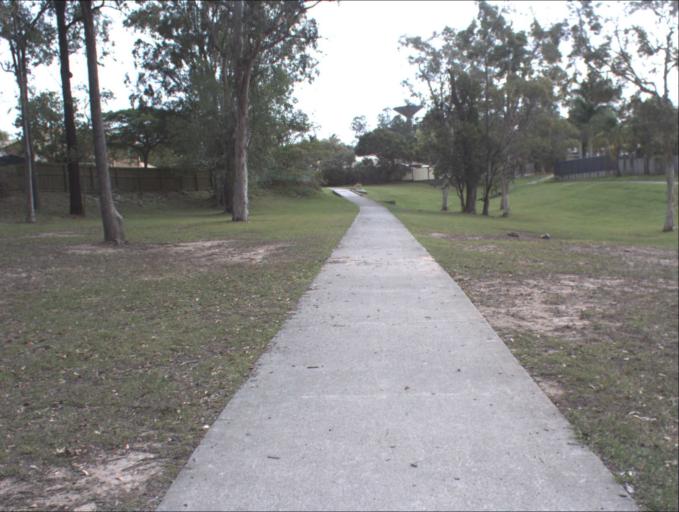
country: AU
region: Queensland
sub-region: Logan
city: Park Ridge South
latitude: -27.6757
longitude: 153.0361
